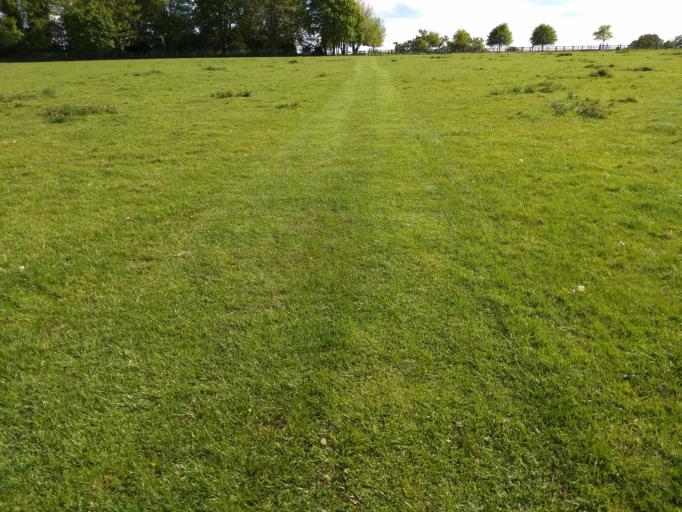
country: GB
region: England
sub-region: Milton Keynes
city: Castlethorpe
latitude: 52.0695
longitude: -0.8207
